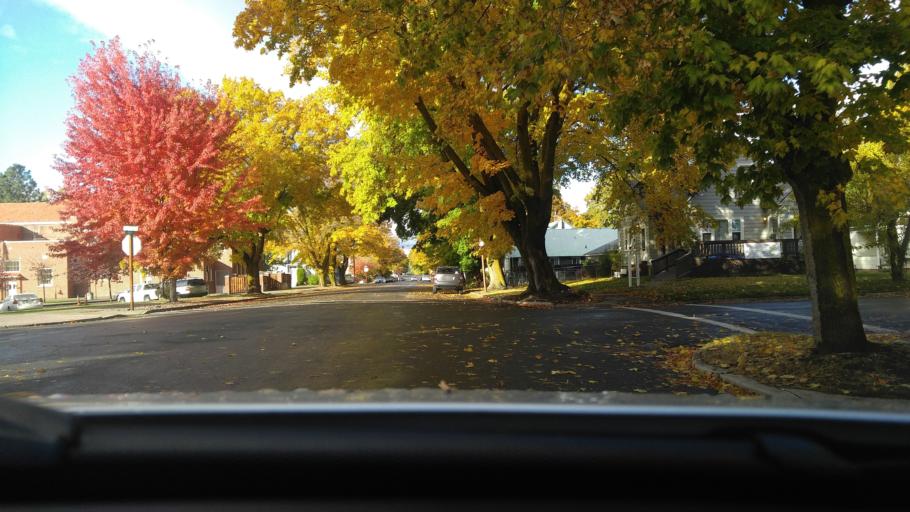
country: US
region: Washington
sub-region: Kittitas County
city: Ellensburg
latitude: 46.9978
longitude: -120.5418
